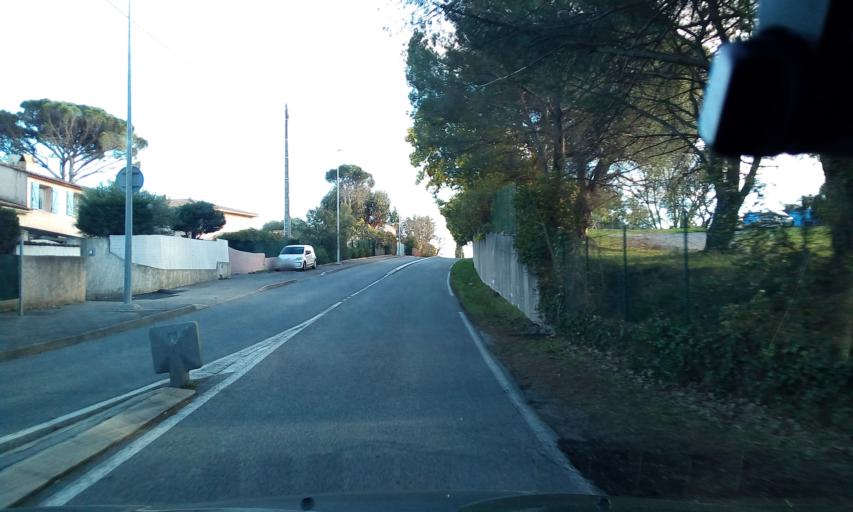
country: FR
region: Provence-Alpes-Cote d'Azur
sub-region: Departement du Var
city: Saint-Raphael
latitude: 43.4411
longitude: 6.7670
